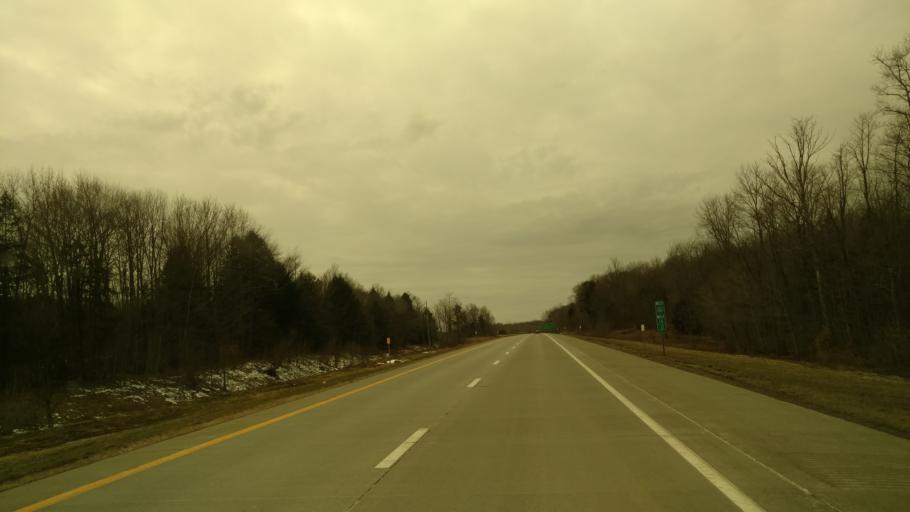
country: US
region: New York
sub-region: Chautauqua County
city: Mayville
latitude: 42.1564
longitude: -79.4615
